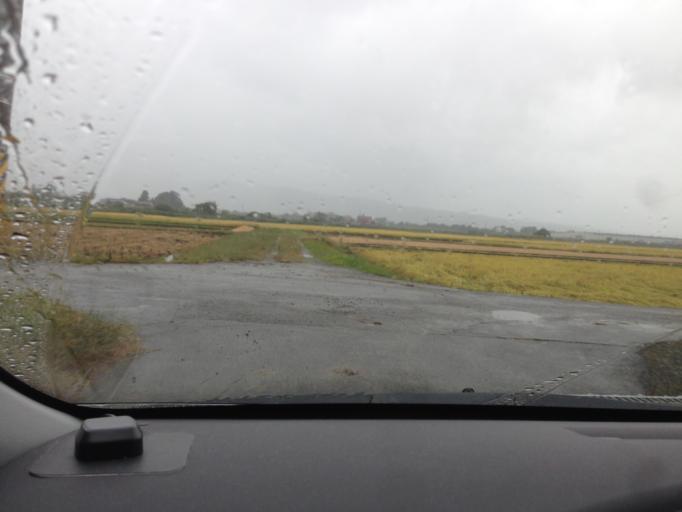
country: JP
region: Fukushima
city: Kitakata
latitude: 37.4619
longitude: 139.8650
